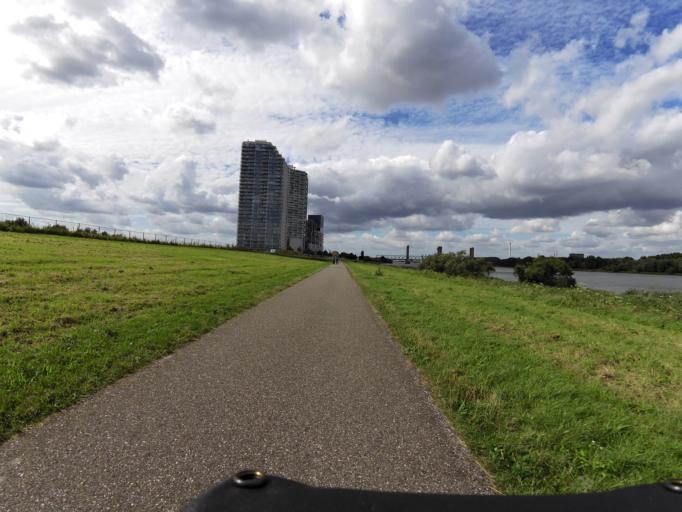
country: NL
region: South Holland
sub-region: Gemeente Spijkenisse
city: Spijkenisse
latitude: 51.8501
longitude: 4.3469
